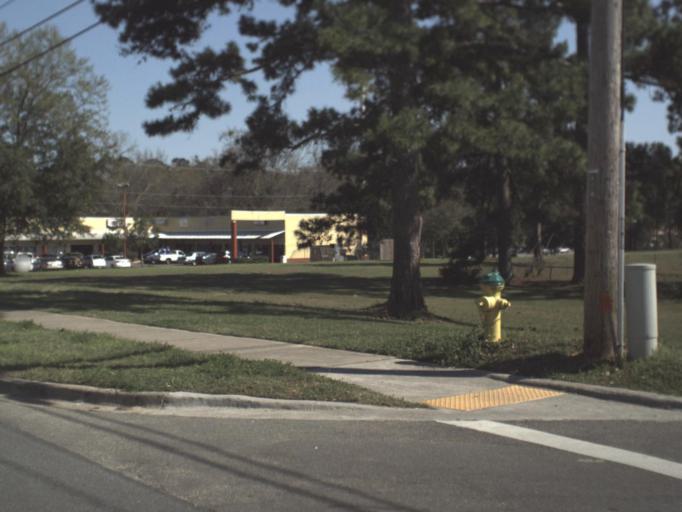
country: US
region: Florida
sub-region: Leon County
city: Tallahassee
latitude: 30.4407
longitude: -84.3215
